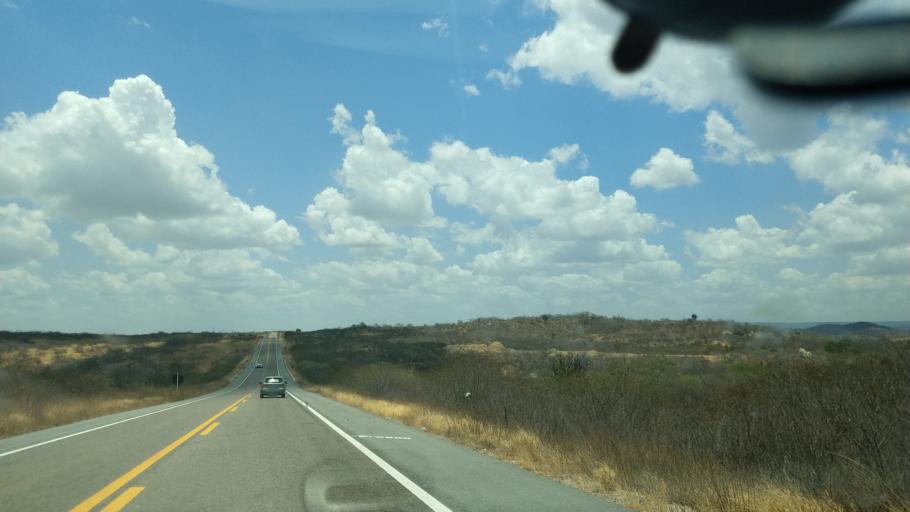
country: BR
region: Rio Grande do Norte
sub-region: Cerro Cora
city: Cerro Cora
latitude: -6.2040
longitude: -36.3269
